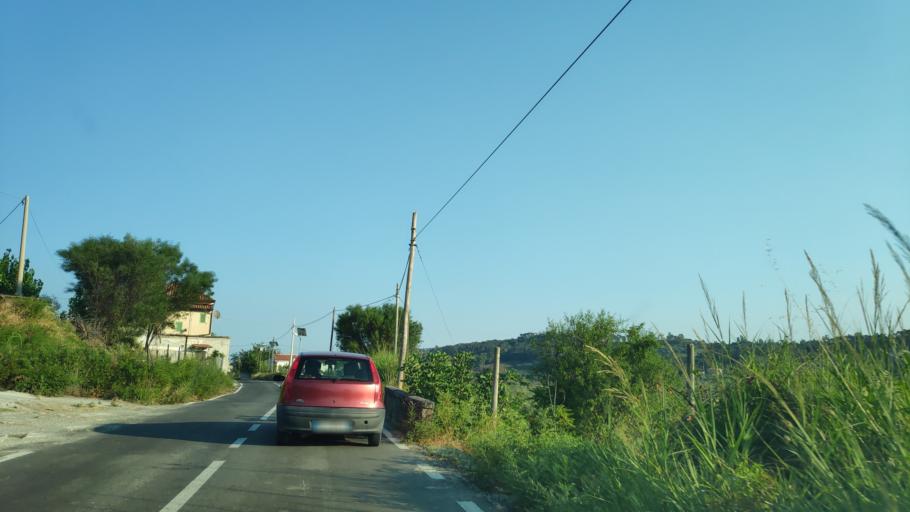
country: IT
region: Calabria
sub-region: Provincia di Reggio Calabria
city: Caulonia Marina
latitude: 38.3701
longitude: 16.4468
